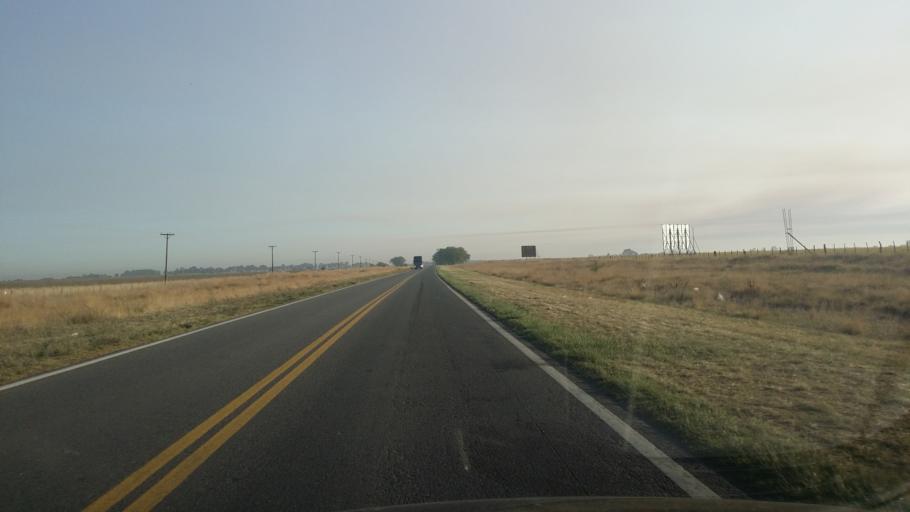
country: AR
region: La Pampa
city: Santa Rosa
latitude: -36.5004
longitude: -64.2801
